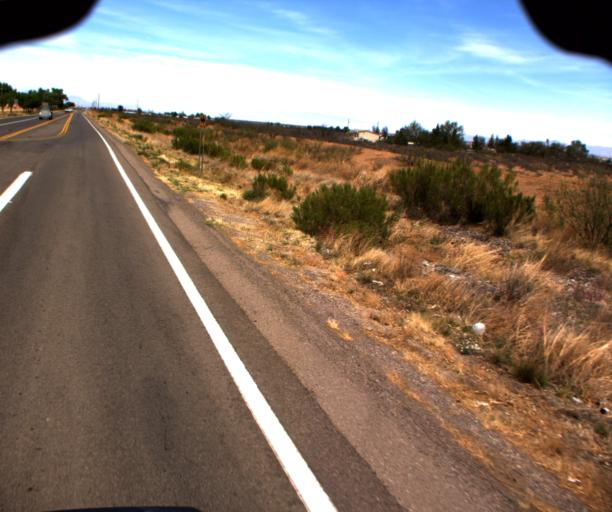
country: US
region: Arizona
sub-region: Cochise County
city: Willcox
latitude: 31.9417
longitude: -109.8316
